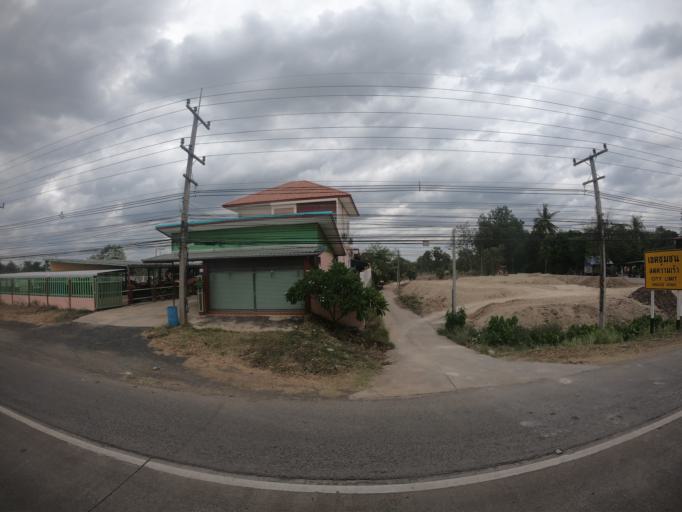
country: TH
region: Nakhon Ratchasima
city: Nakhon Ratchasima
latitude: 14.8698
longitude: 102.1815
